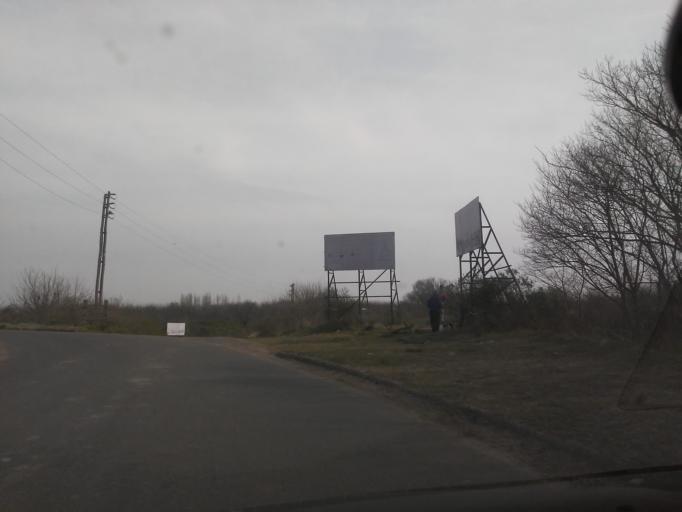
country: AR
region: Buenos Aires
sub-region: Partido de Marcos Paz
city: Marcos Paz
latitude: -34.6748
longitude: -58.8625
